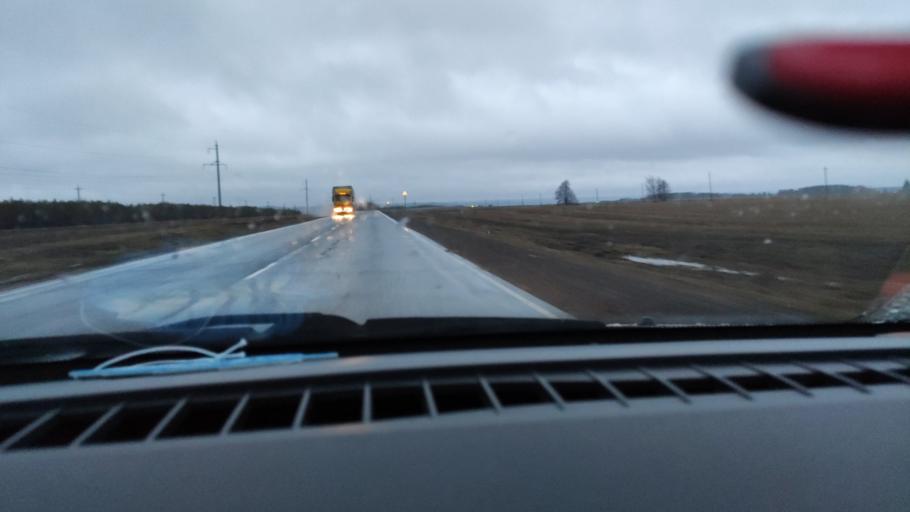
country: RU
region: Udmurtiya
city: Alnashi
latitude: 56.2038
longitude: 52.4481
